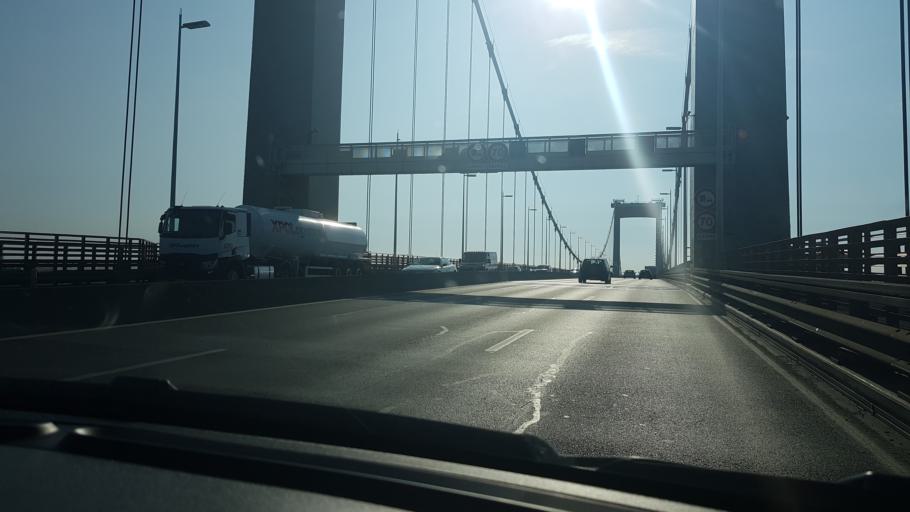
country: FR
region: Aquitaine
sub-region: Departement de la Gironde
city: Lormont
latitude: 44.8803
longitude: -0.5394
